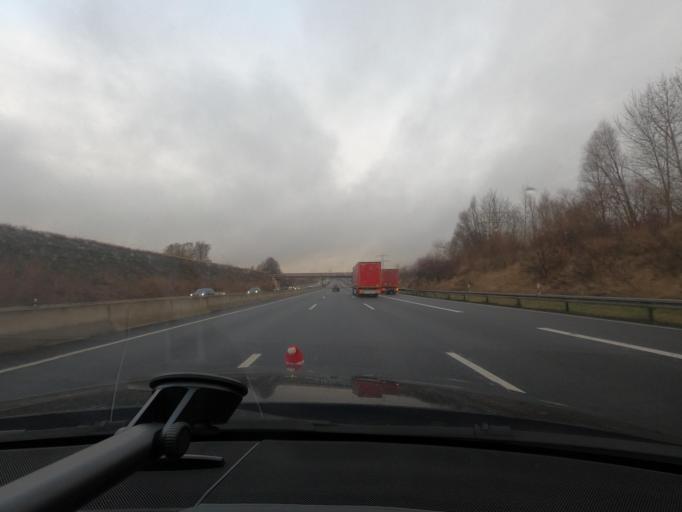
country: DE
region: Lower Saxony
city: Goettingen
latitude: 51.5519
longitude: 9.8794
